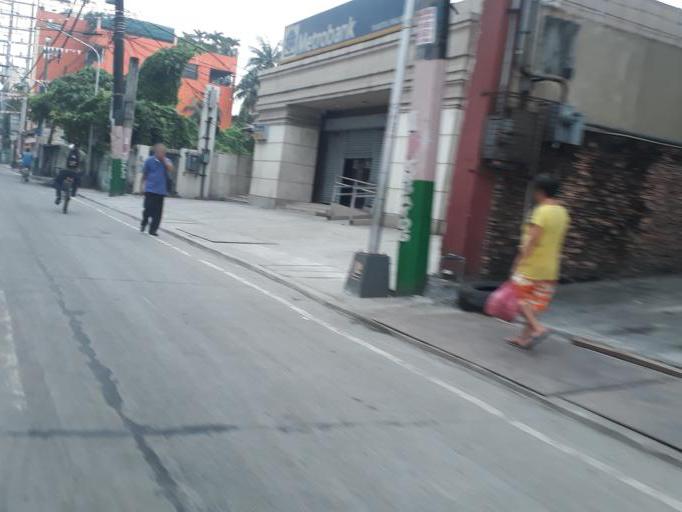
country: PH
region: Metro Manila
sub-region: Caloocan City
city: Niugan
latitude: 14.6672
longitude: 120.9662
